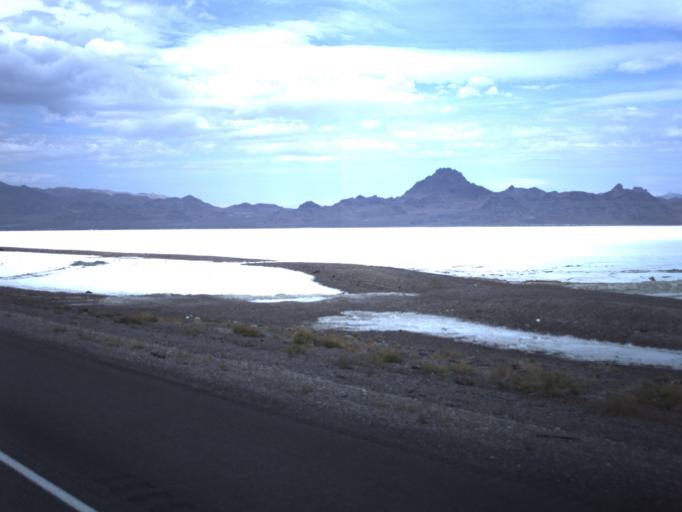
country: US
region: Utah
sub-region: Tooele County
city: Wendover
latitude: 40.7405
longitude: -113.9075
